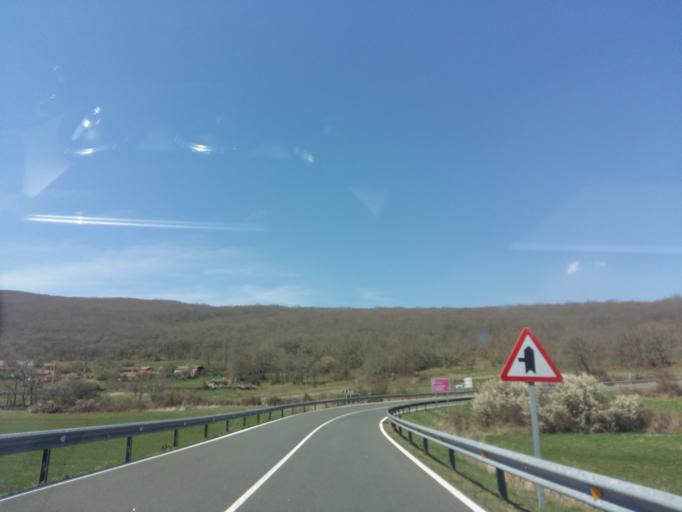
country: ES
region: Cantabria
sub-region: Provincia de Cantabria
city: Mataporquera
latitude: 42.8987
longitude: -4.1907
